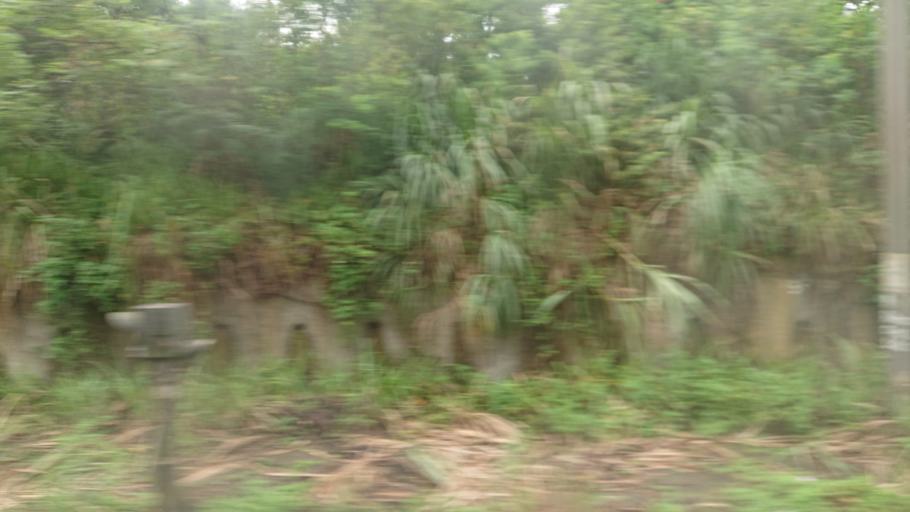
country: TW
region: Taiwan
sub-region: Keelung
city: Keelung
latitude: 25.0979
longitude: 121.7205
